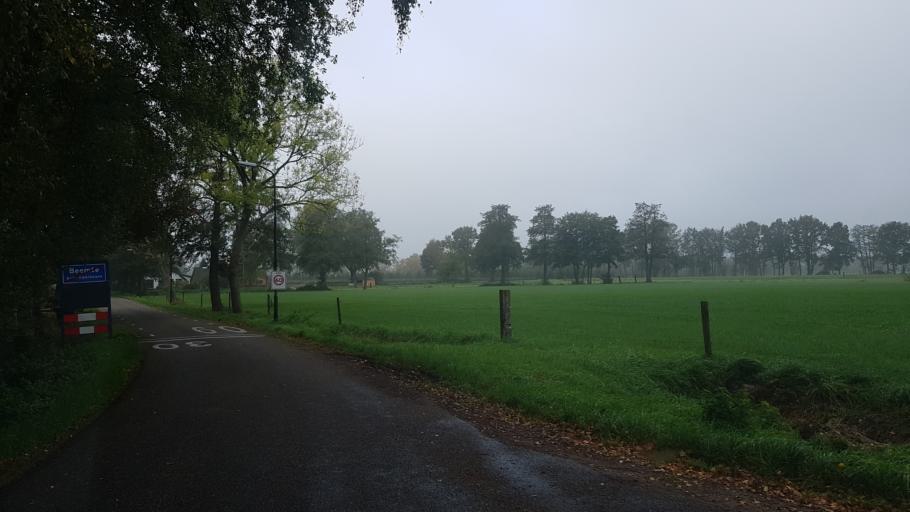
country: NL
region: Gelderland
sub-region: Gemeente Epe
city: Vaassen
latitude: 52.2569
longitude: 5.9893
